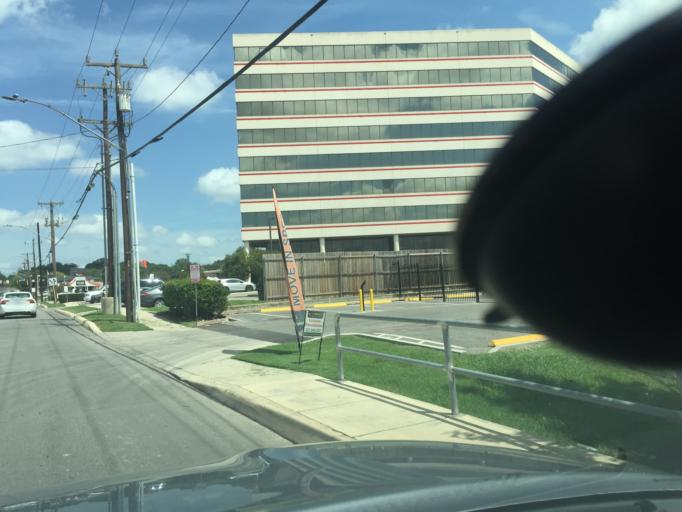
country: US
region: Texas
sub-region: Bexar County
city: Castle Hills
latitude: 29.5302
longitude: -98.4951
